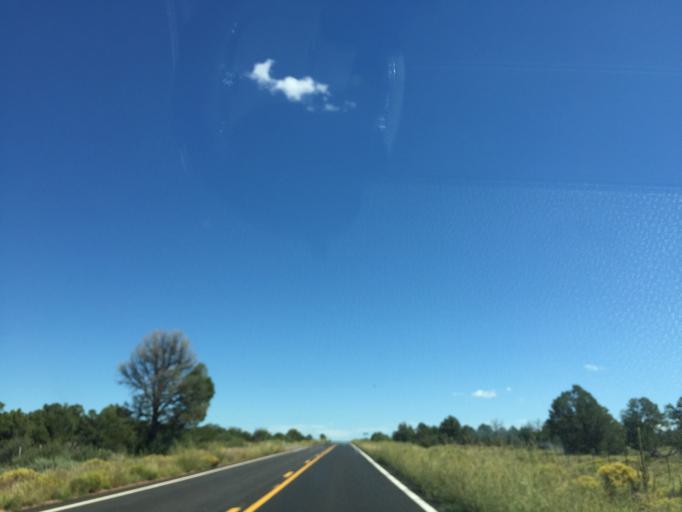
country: US
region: Arizona
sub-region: Coconino County
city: Parks
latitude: 35.6097
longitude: -112.0606
